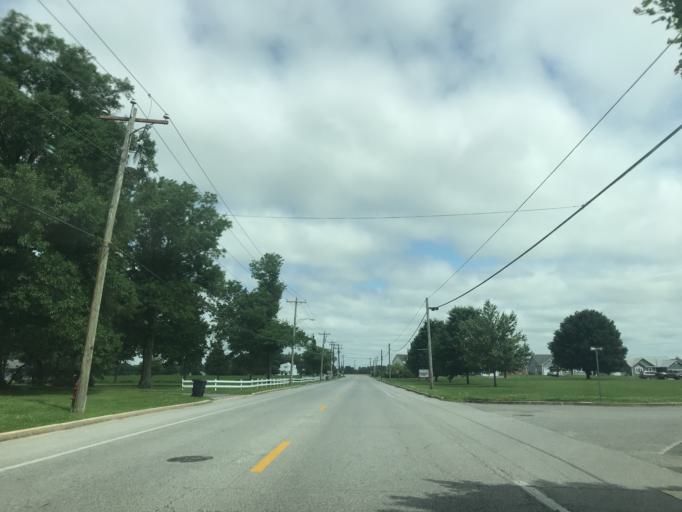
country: US
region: Maryland
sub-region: Caroline County
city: Ridgely
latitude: 38.9513
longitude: -75.8856
